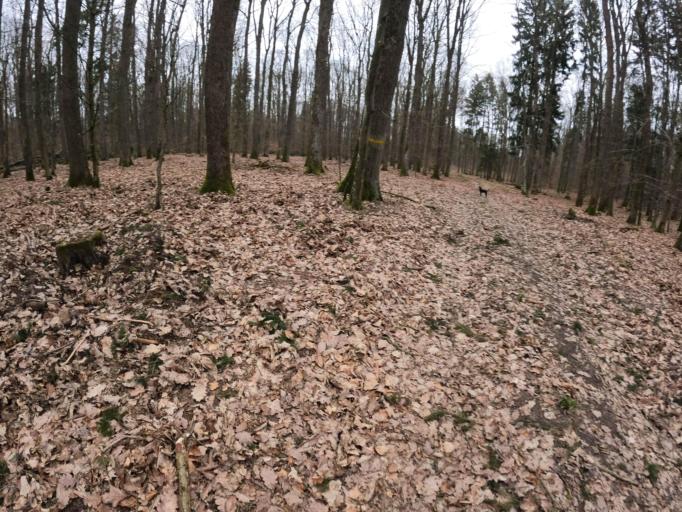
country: PL
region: West Pomeranian Voivodeship
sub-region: Powiat kamienski
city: Golczewo
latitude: 53.8116
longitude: 15.0217
